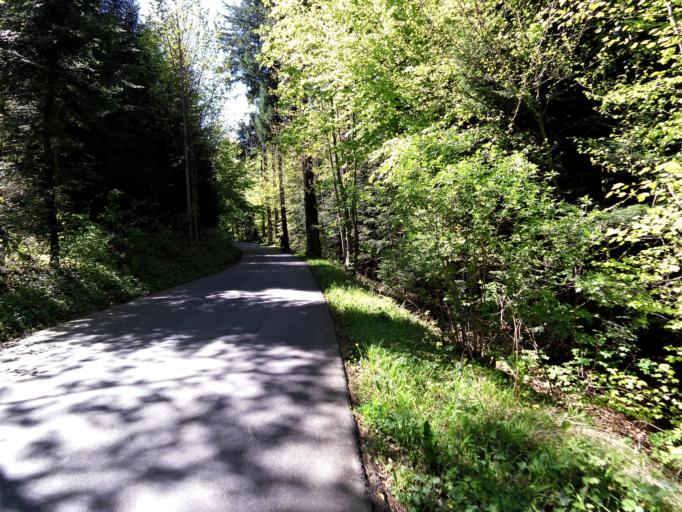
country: CH
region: Thurgau
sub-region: Weinfelden District
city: Berg
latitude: 47.5835
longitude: 9.1434
